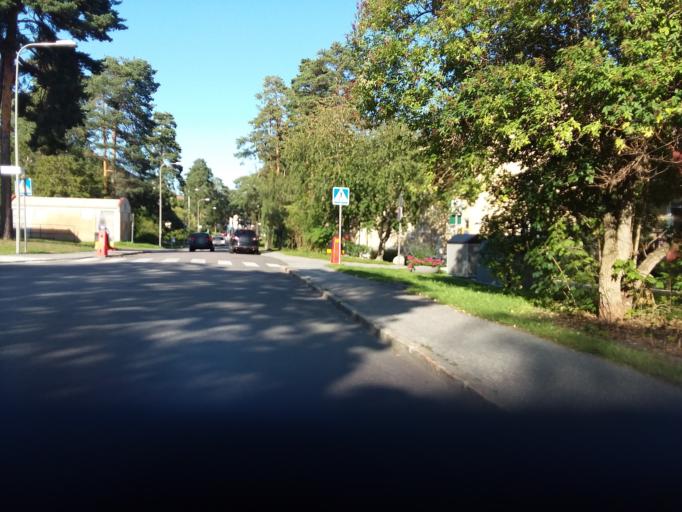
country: SE
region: Stockholm
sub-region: Stockholms Kommun
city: Bromma
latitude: 59.3475
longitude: 17.8773
